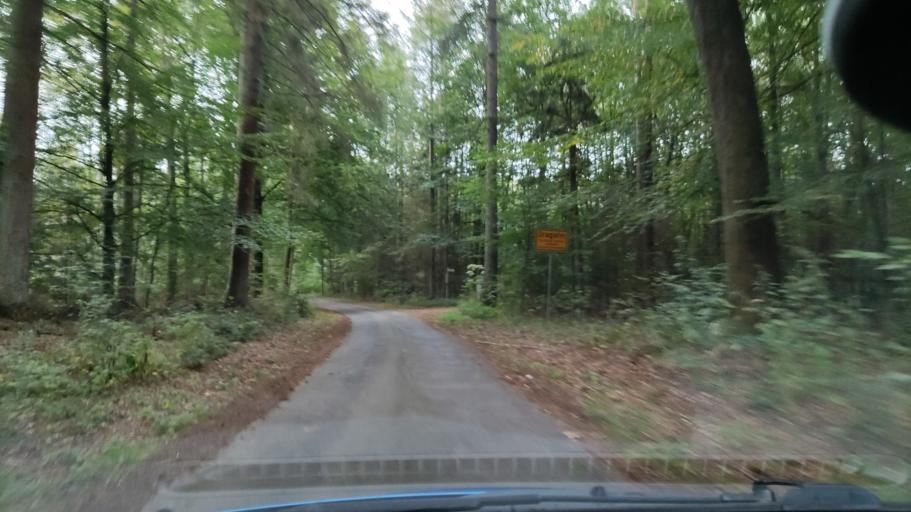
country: DE
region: Lower Saxony
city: Karwitz
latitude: 53.0908
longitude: 10.9787
